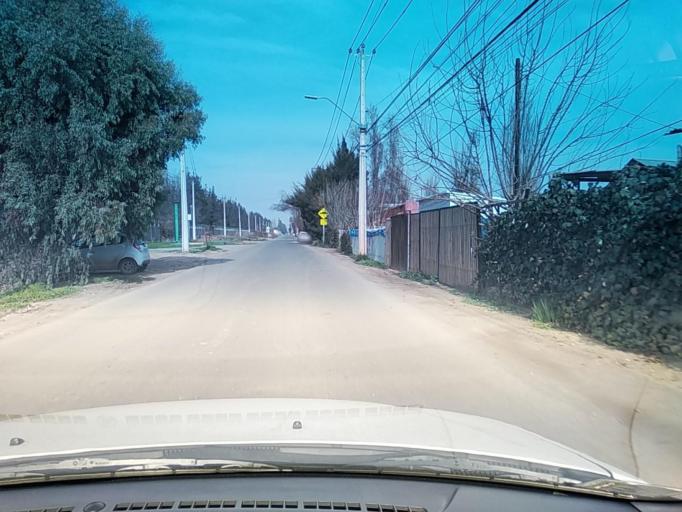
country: CL
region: Santiago Metropolitan
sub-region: Provincia de Chacabuco
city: Chicureo Abajo
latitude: -33.2862
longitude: -70.7294
